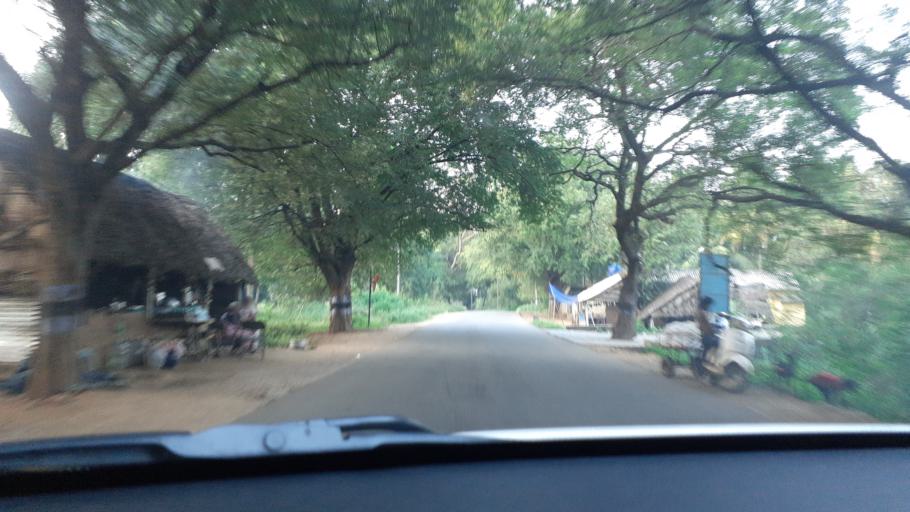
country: IN
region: Tamil Nadu
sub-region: Dindigul
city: Ayakudi
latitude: 10.4055
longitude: 77.5442
